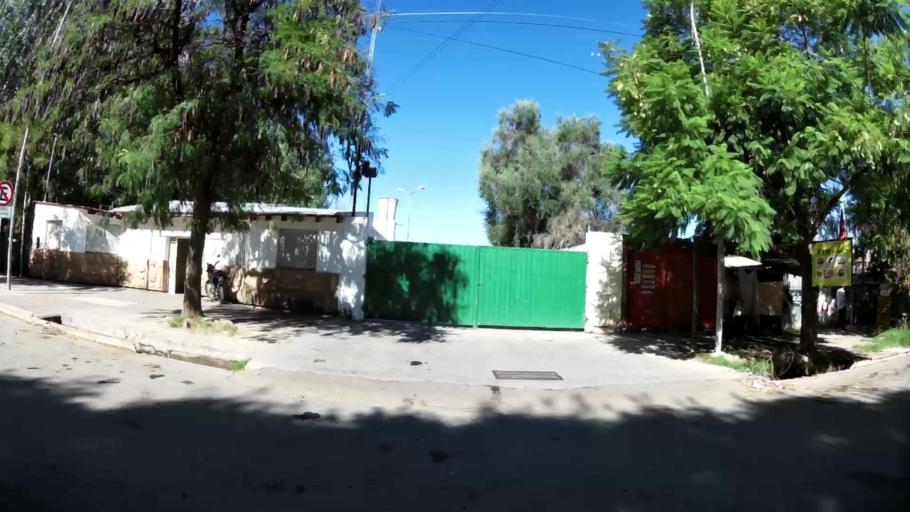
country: AR
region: Mendoza
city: Las Heras
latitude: -32.8441
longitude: -68.8199
